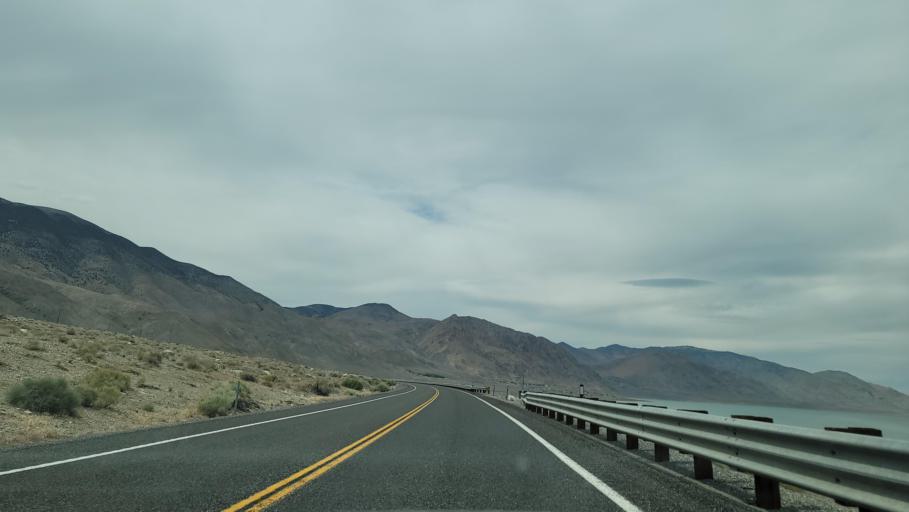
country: US
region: Nevada
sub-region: Mineral County
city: Hawthorne
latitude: 38.6101
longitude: -118.7161
